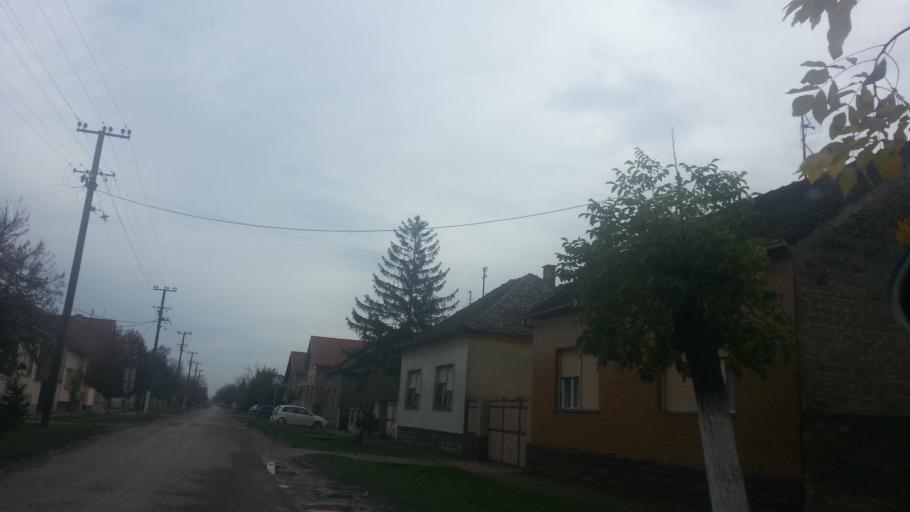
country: RS
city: Golubinci
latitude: 44.9860
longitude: 20.0656
